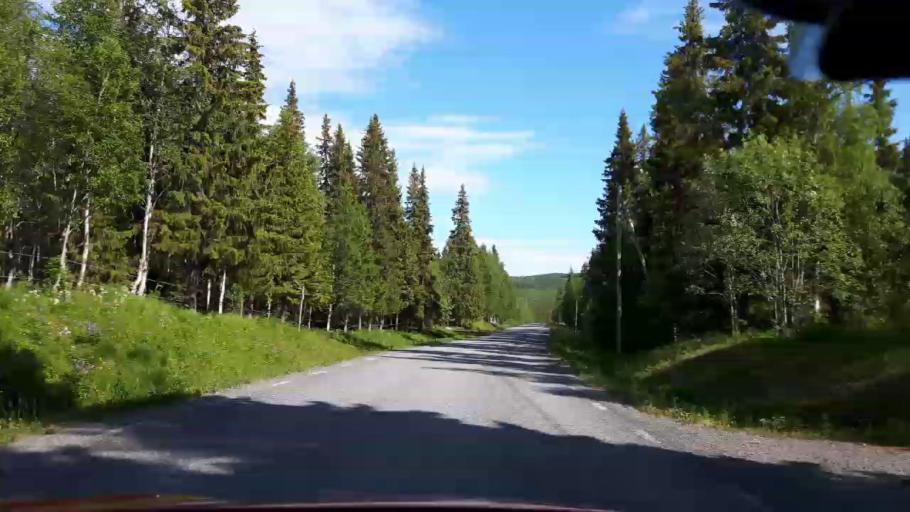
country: SE
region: Jaemtland
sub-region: Krokoms Kommun
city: Valla
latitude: 63.7598
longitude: 14.1005
